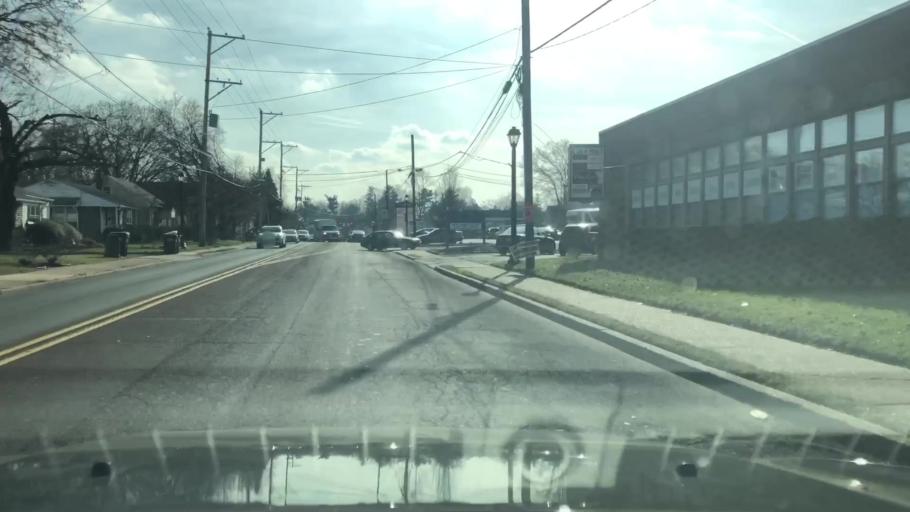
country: US
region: Pennsylvania
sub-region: Bucks County
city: Langhorne
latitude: 40.1787
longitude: -74.9180
